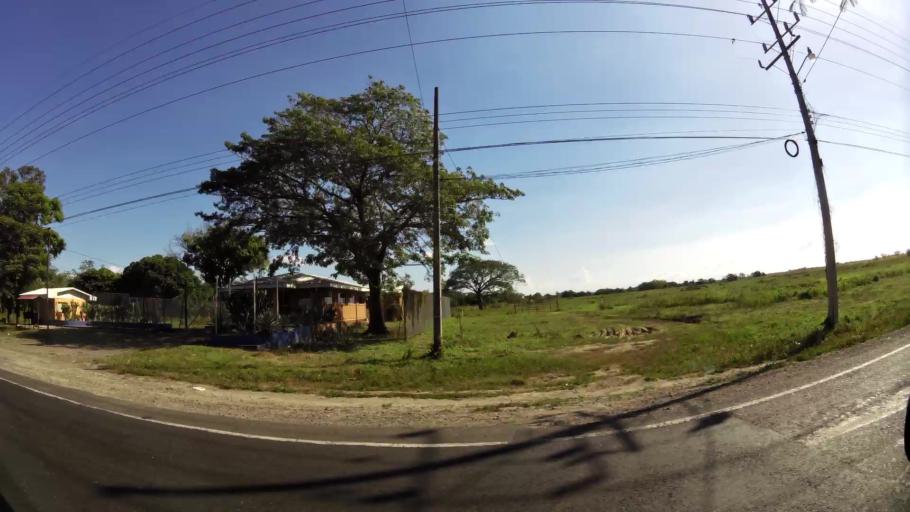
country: CR
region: Guanacaste
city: Liberia
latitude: 10.6150
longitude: -85.4770
